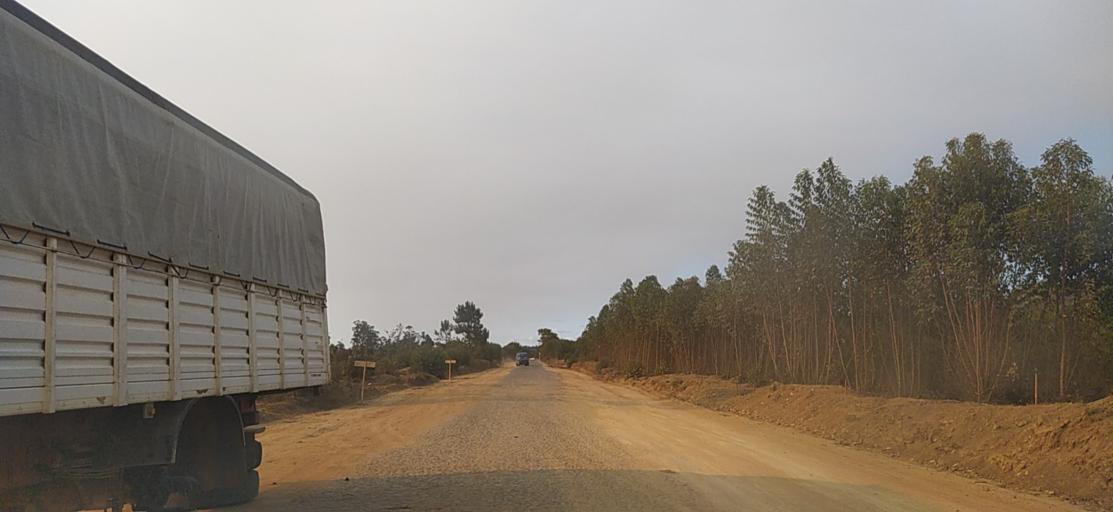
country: MG
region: Alaotra Mangoro
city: Moramanga
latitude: -18.6181
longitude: 48.2767
